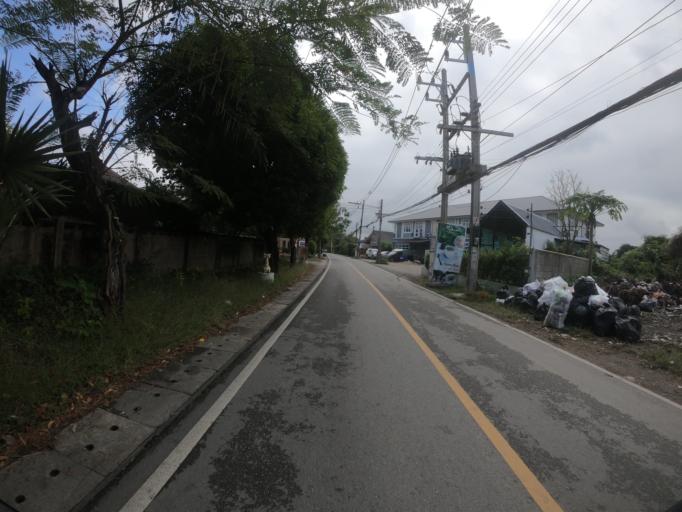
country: TH
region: Chiang Mai
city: Hang Dong
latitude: 18.7263
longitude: 98.9503
